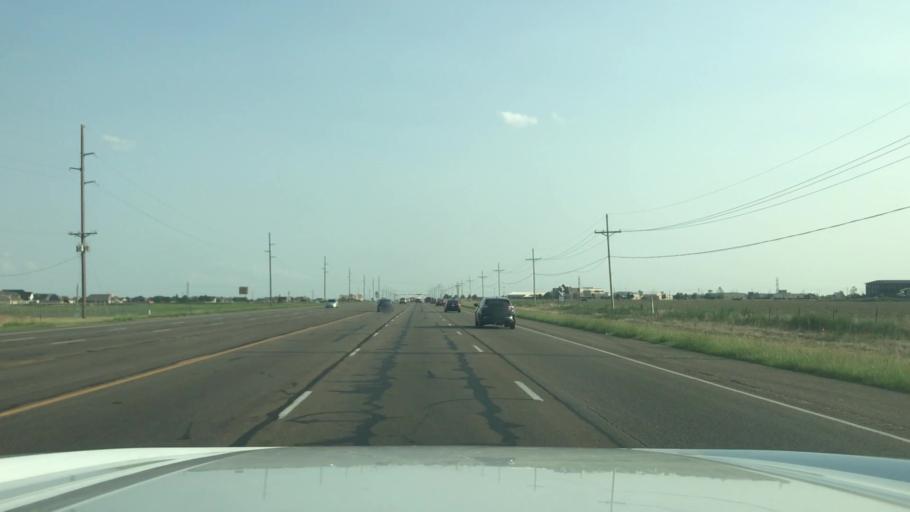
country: US
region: Texas
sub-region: Potter County
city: Amarillo
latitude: 35.1549
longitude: -101.9383
